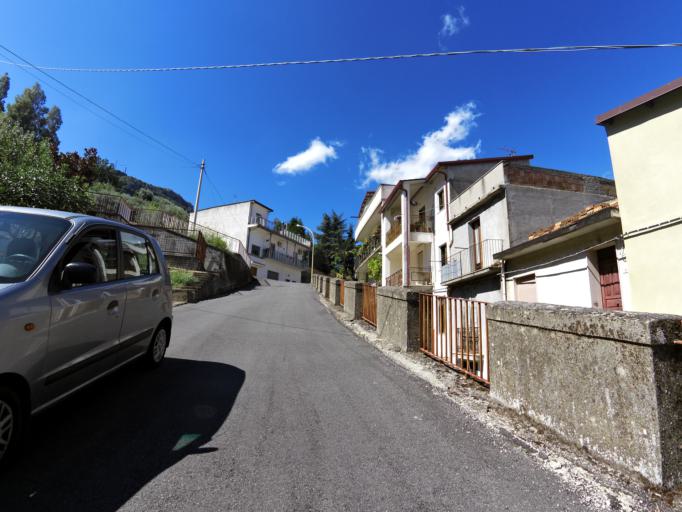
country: IT
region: Calabria
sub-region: Provincia di Reggio Calabria
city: Bivongi
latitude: 38.4806
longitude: 16.4522
